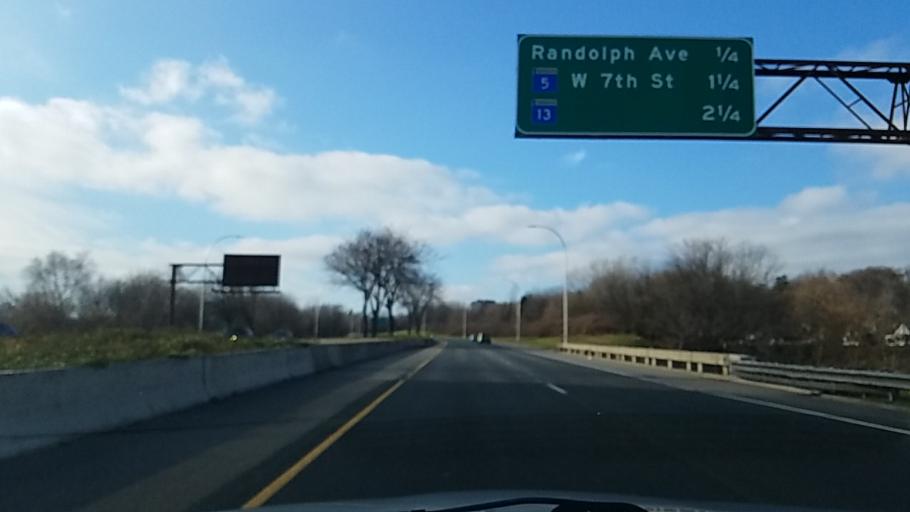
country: US
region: Minnesota
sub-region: Dakota County
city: West Saint Paul
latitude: 44.9316
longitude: -93.1358
